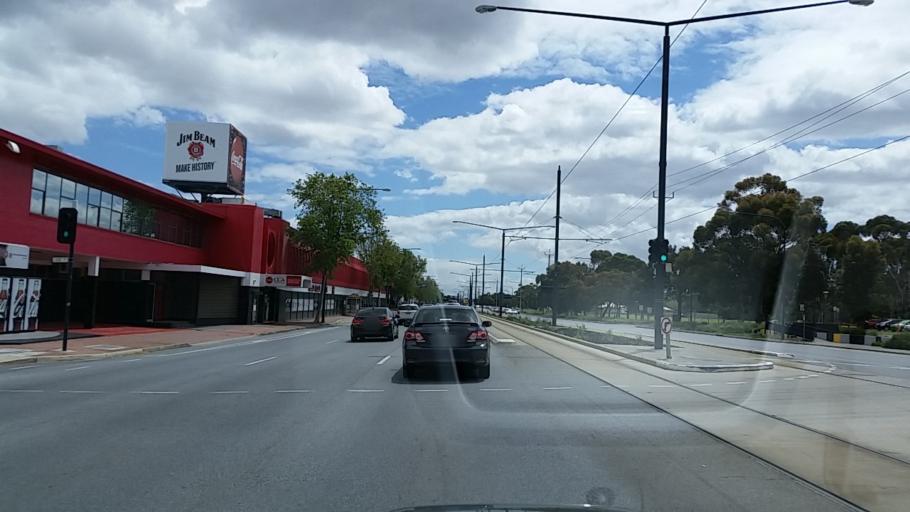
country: AU
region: South Australia
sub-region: City of West Torrens
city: Thebarton
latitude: -34.9174
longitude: 138.5784
